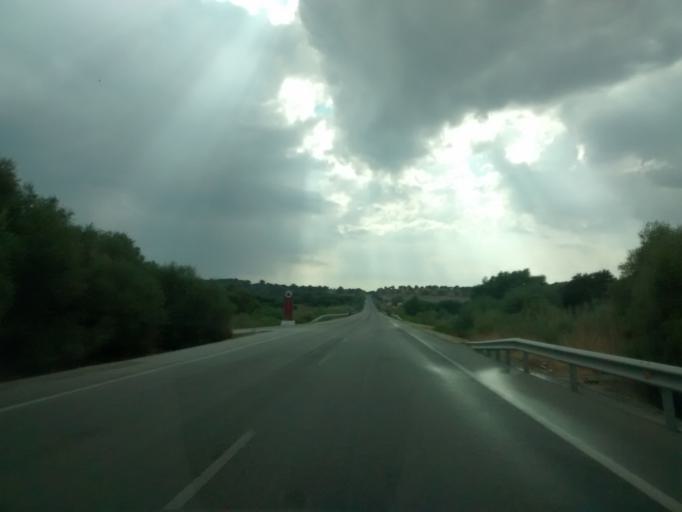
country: ES
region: Andalusia
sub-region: Provincia de Cadiz
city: Prado del Rey
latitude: 36.7463
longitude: -5.6218
